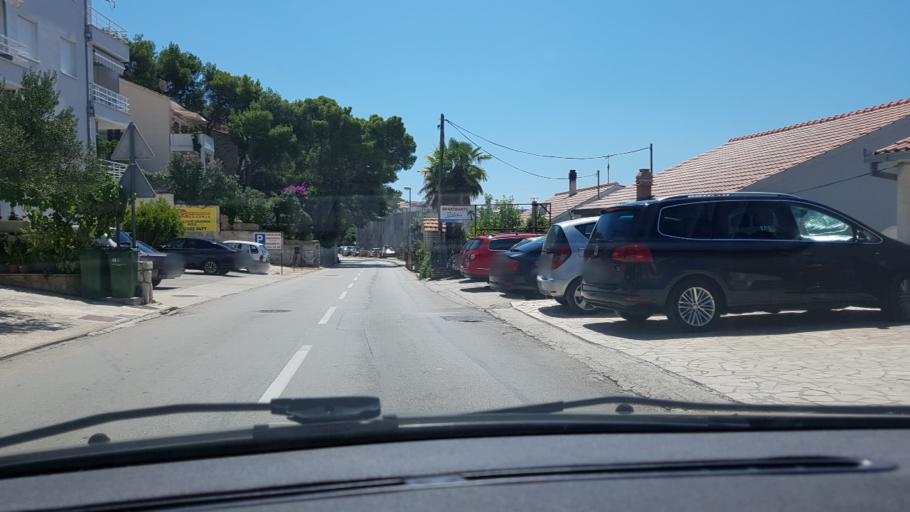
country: HR
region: Splitsko-Dalmatinska
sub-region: Grad Trogir
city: Trogir
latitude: 43.5095
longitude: 16.2560
